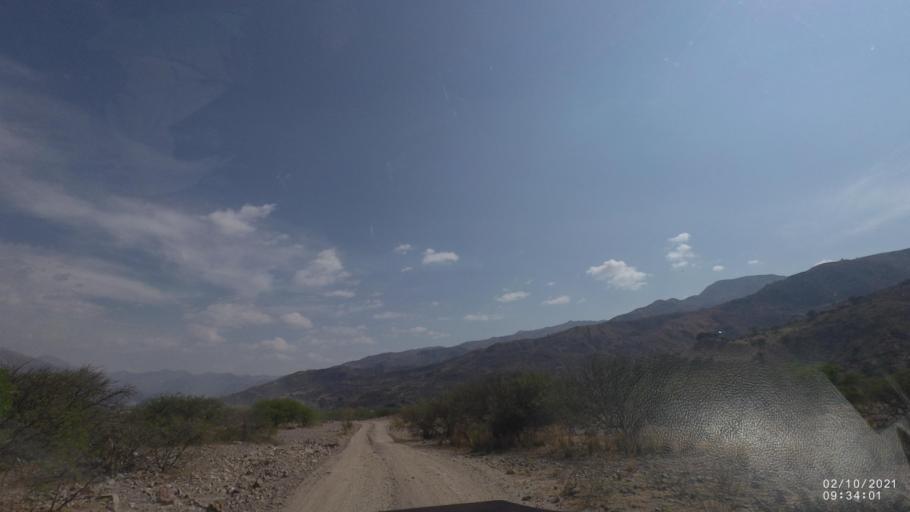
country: BO
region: Cochabamba
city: Irpa Irpa
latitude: -17.8418
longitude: -66.3193
